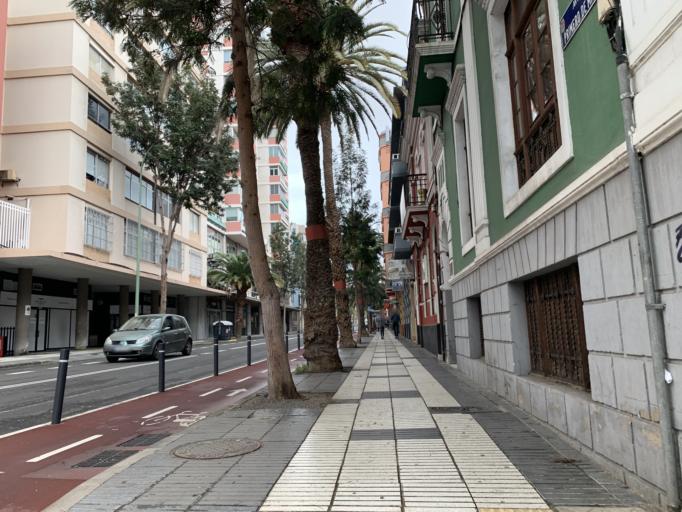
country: ES
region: Canary Islands
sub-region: Provincia de Las Palmas
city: Las Palmas de Gran Canaria
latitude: 28.1053
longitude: -15.4197
